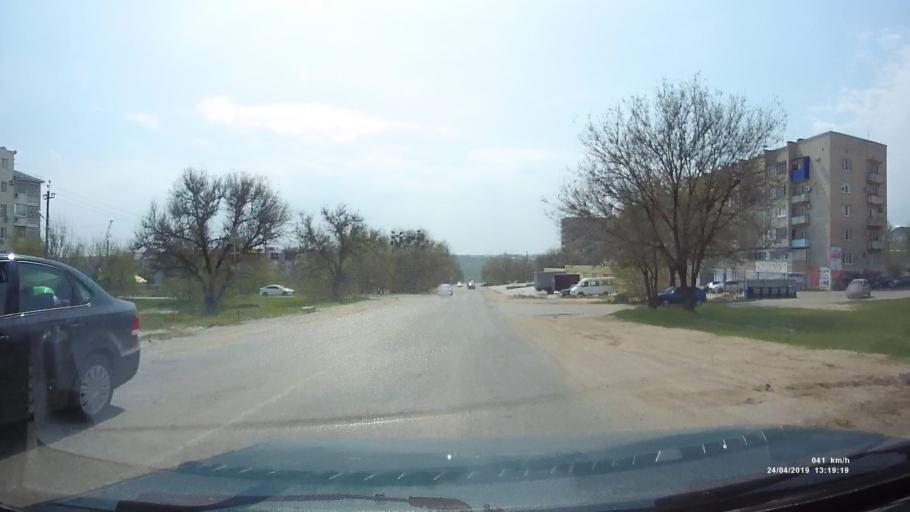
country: RU
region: Kalmykiya
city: Elista
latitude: 46.3006
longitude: 44.2916
